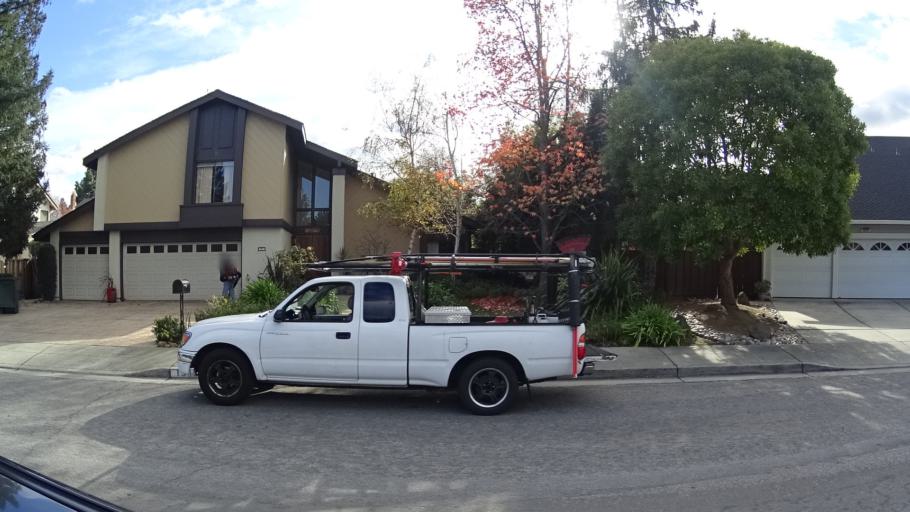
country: US
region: California
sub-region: Santa Clara County
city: Sunnyvale
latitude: 37.3512
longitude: -122.0585
